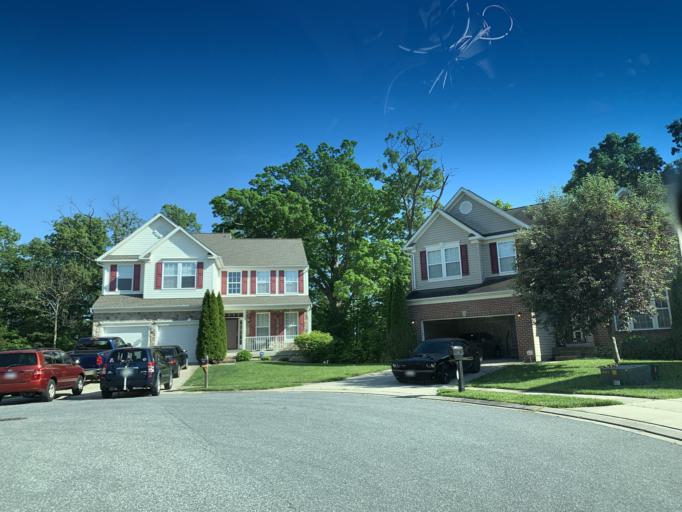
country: US
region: Maryland
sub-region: Harford County
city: Riverside
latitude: 39.4807
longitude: -76.2372
